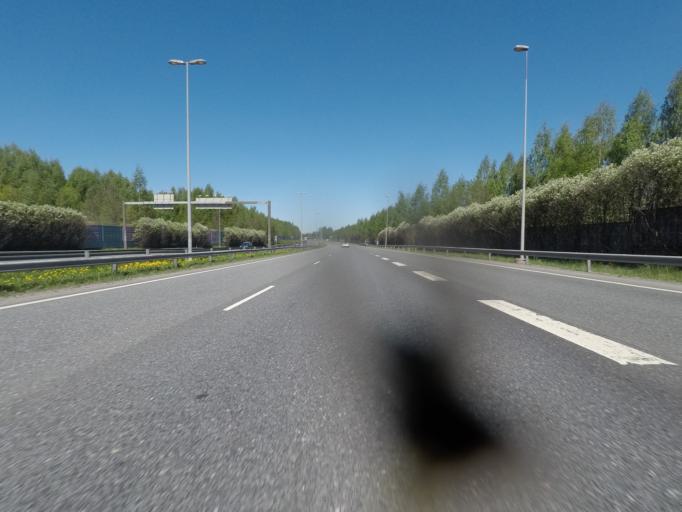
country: FI
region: Haeme
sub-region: Haemeenlinna
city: Haemeenlinna
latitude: 60.9760
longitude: 24.4713
